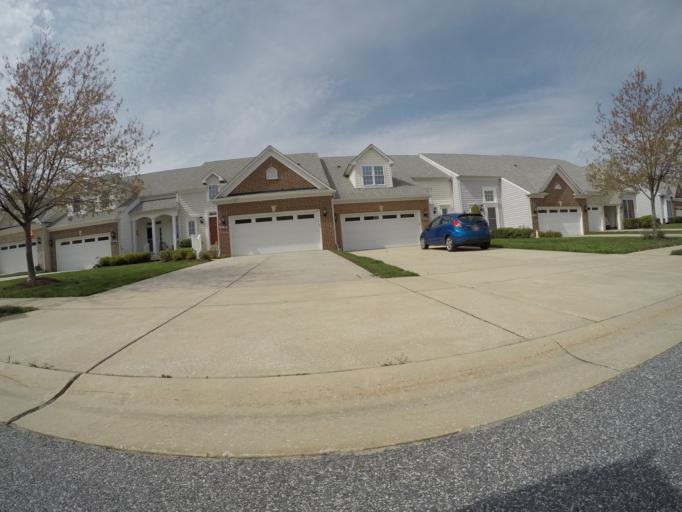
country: US
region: Maryland
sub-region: Howard County
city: Ellicott City
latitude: 39.2506
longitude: -76.7872
